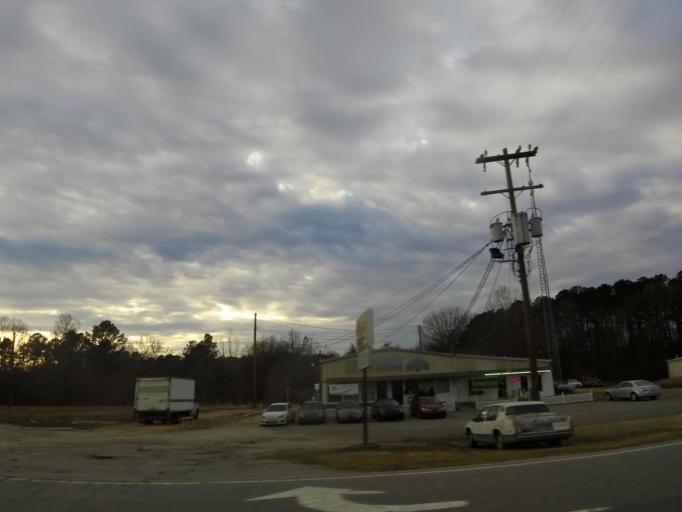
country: US
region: North Carolina
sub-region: Nash County
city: Rocky Mount
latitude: 35.9188
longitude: -77.8317
